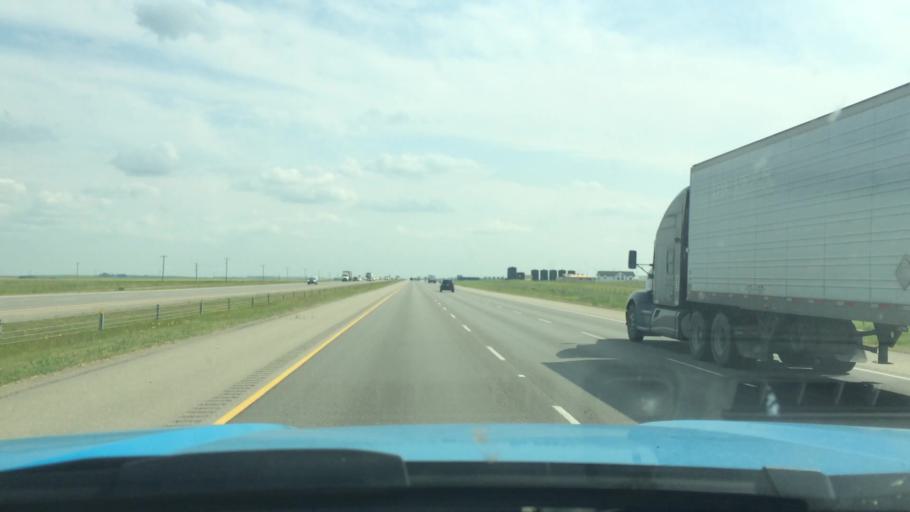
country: CA
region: Alberta
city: Crossfield
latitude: 51.5075
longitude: -114.0254
